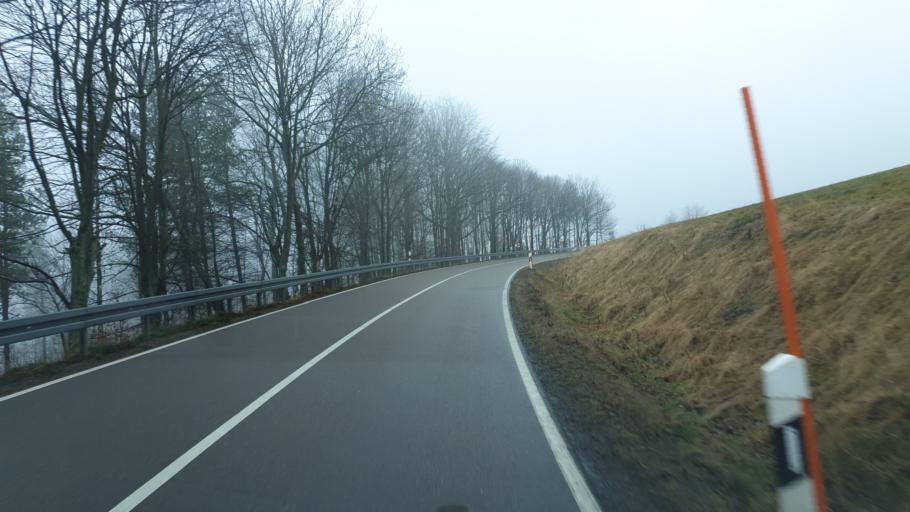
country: DE
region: Saxony
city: Neuhausen
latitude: 50.6600
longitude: 13.4776
